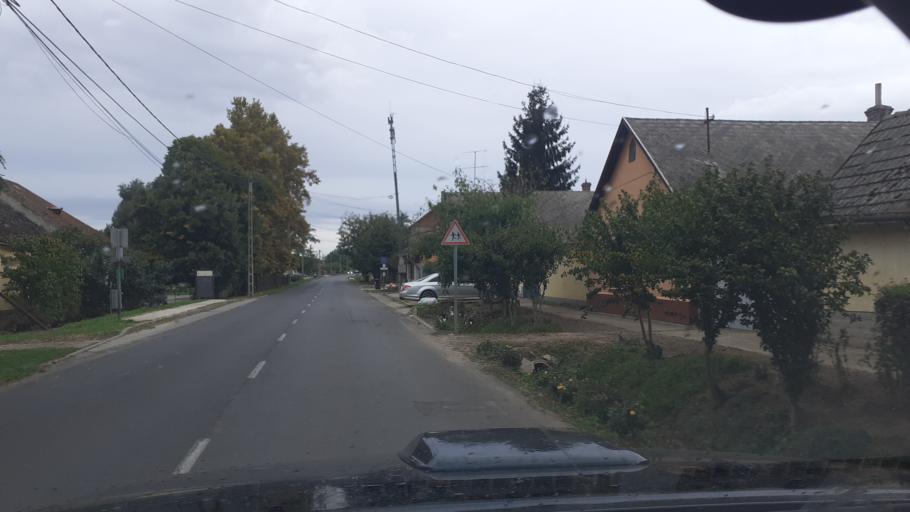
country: HU
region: Tolna
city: Dunafoldvar
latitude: 46.7944
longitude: 18.9336
